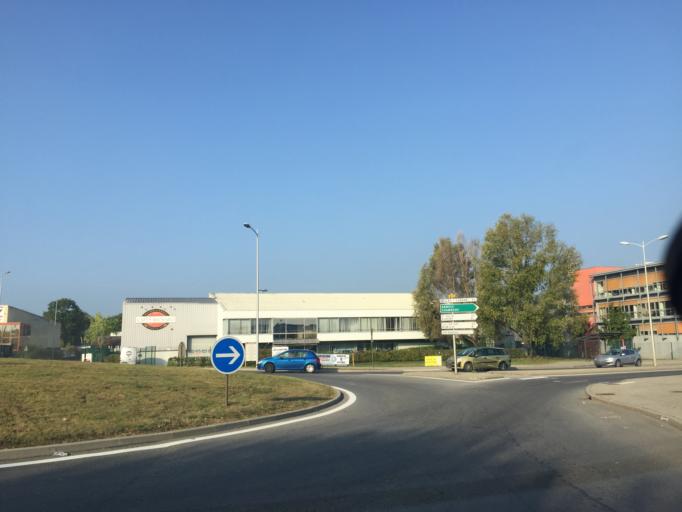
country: FR
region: Rhone-Alpes
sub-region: Departement de la Haute-Savoie
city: Alby-sur-Cheran
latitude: 45.8153
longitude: 6.0046
